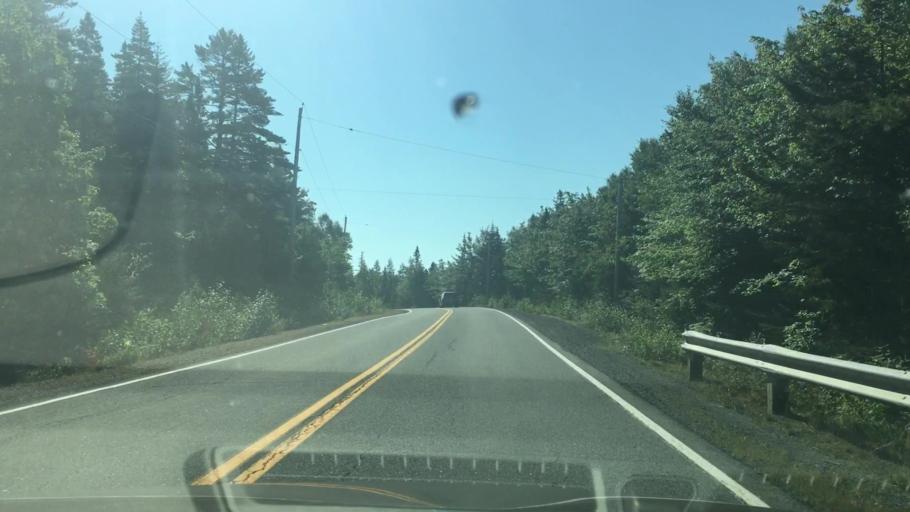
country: CA
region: Nova Scotia
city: Cole Harbour
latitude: 44.8090
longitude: -62.8347
